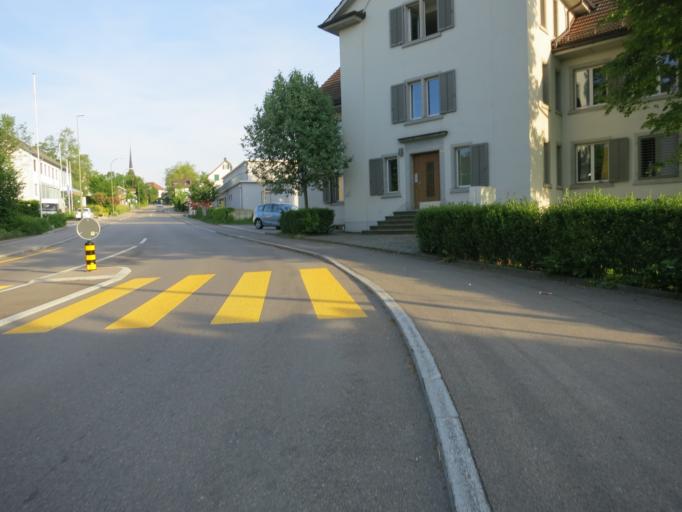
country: CH
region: Zurich
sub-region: Bezirk Hinwil
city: Gossau
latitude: 47.3045
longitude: 8.7582
